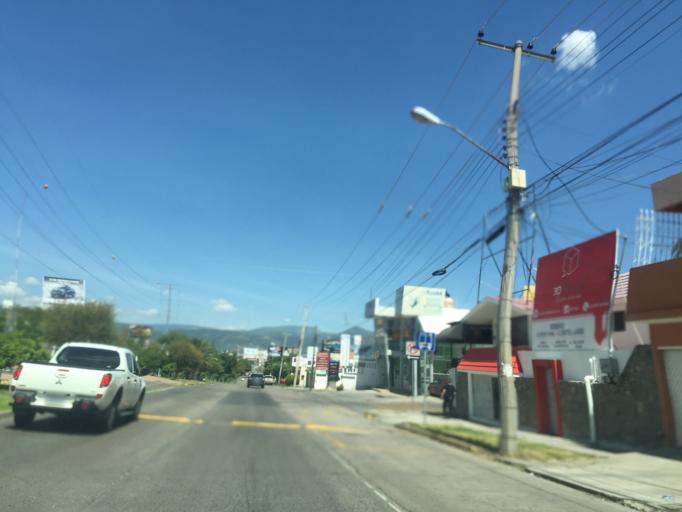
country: MX
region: Guanajuato
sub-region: Leon
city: La Ermita
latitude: 21.1514
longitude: -101.7017
